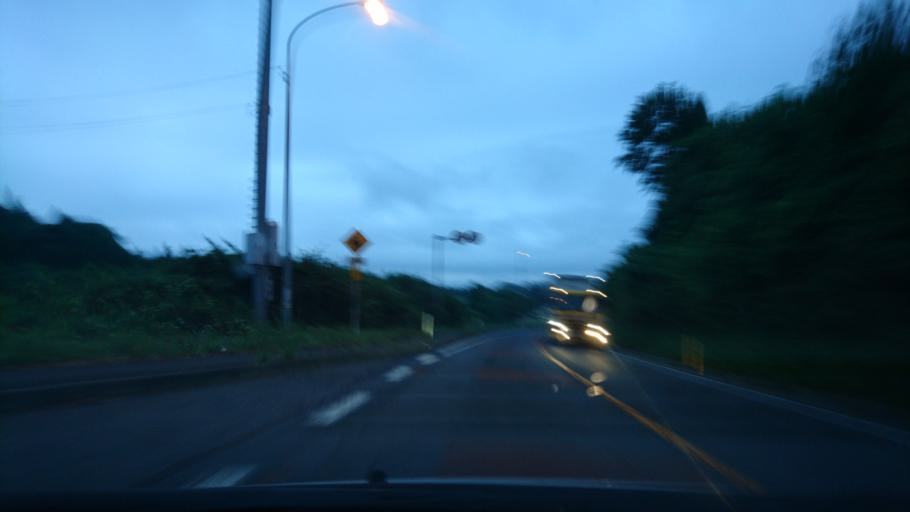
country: JP
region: Iwate
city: Ichinoseki
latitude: 38.8540
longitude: 141.0980
